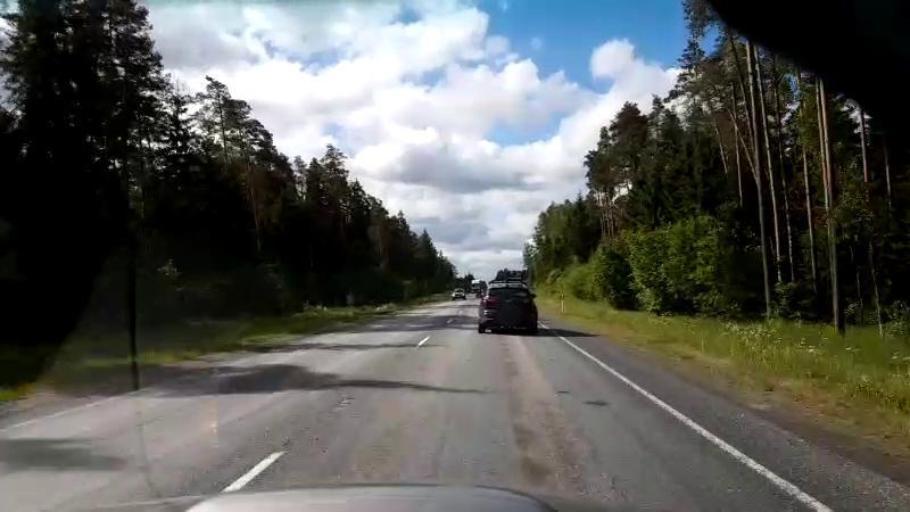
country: EE
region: Harju
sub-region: Saue linn
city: Saue
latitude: 59.1959
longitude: 24.4988
